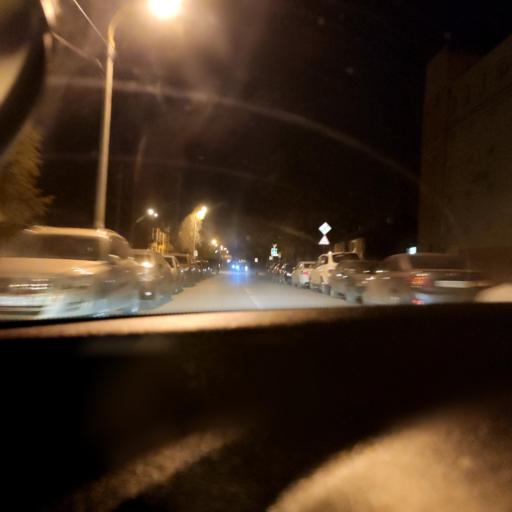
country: RU
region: Samara
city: Samara
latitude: 53.2361
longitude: 50.2565
